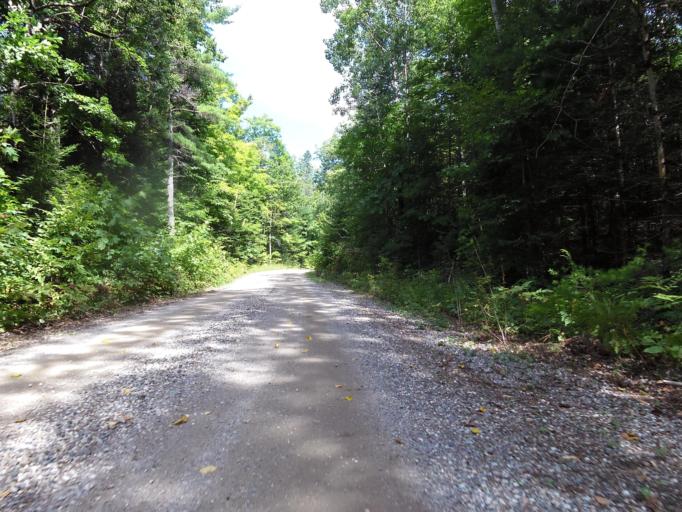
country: CA
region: Ontario
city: Renfrew
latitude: 45.1234
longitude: -76.7198
